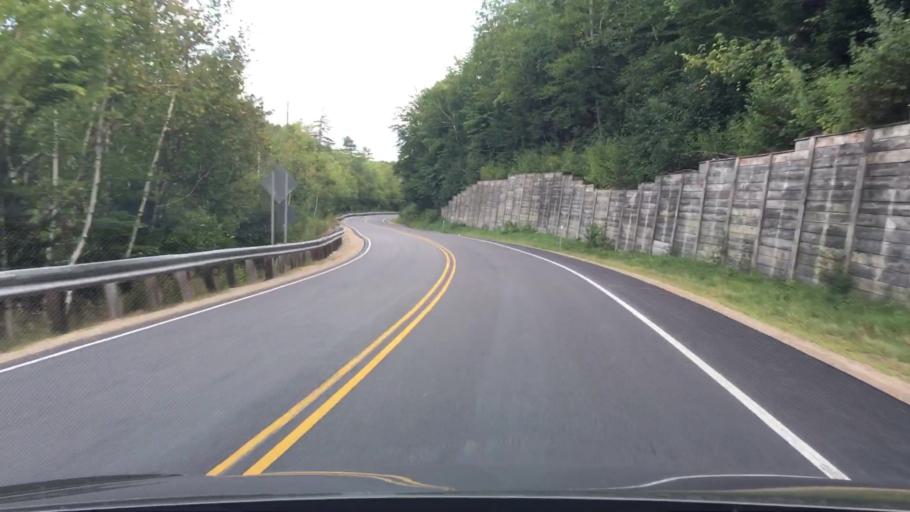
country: US
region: New Hampshire
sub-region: Carroll County
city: Conway
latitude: 43.9933
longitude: -71.2095
